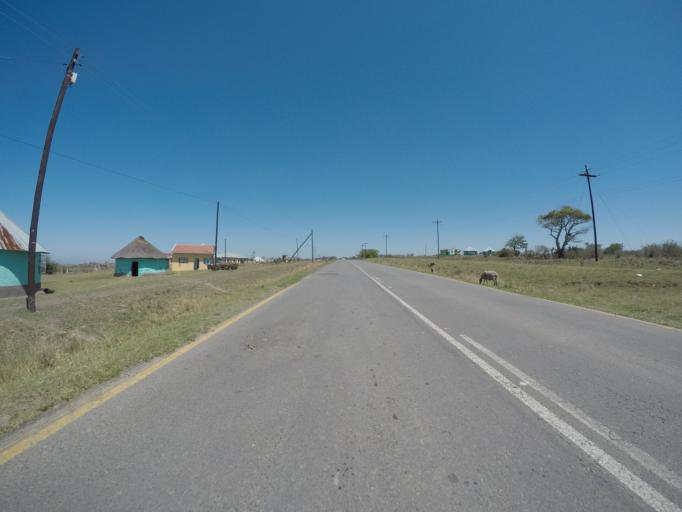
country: ZA
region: Eastern Cape
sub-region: OR Tambo District Municipality
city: Libode
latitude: -31.9093
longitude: 28.9983
